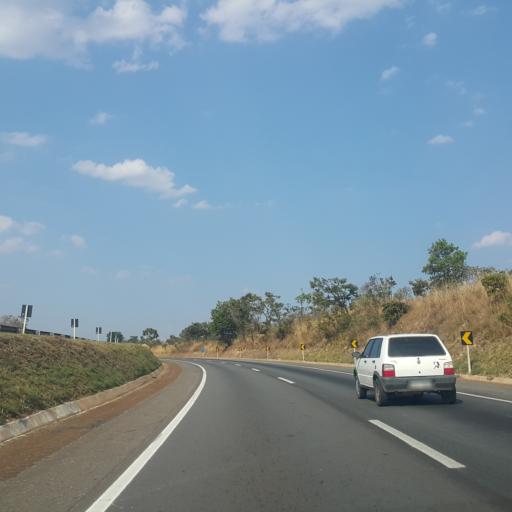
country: BR
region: Goias
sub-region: Abadiania
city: Abadiania
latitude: -16.1147
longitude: -48.5400
